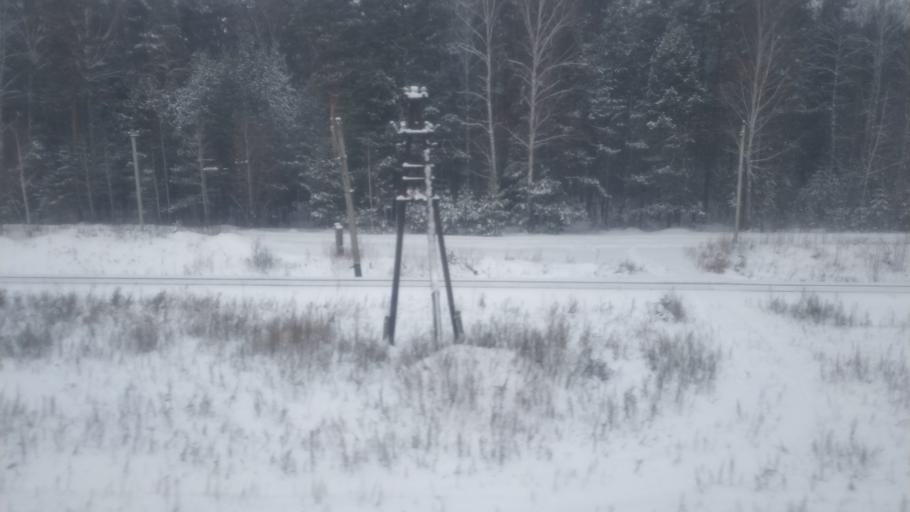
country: RU
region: Udmurtiya
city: Malaya Purga
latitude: 56.5536
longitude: 53.1018
